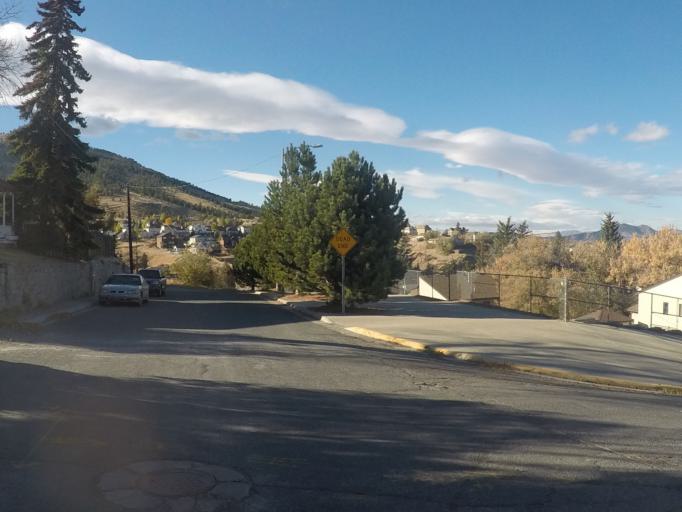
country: US
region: Montana
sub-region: Lewis and Clark County
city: Helena
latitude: 46.5827
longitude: -112.0403
